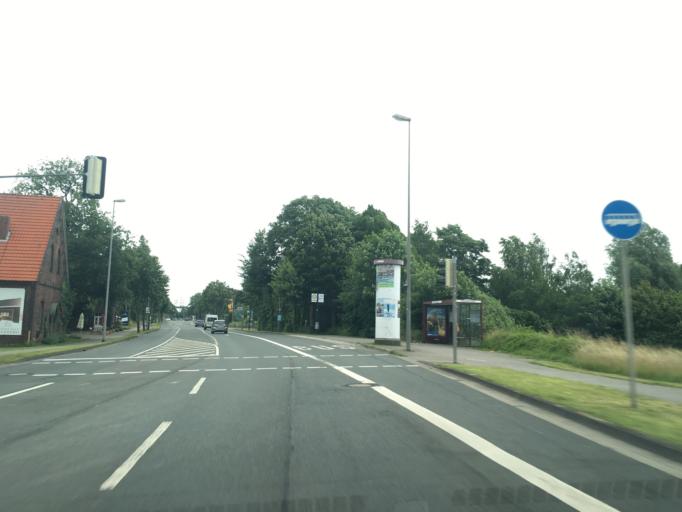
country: DE
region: North Rhine-Westphalia
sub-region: Regierungsbezirk Munster
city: Muenster
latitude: 51.9253
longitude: 7.5792
